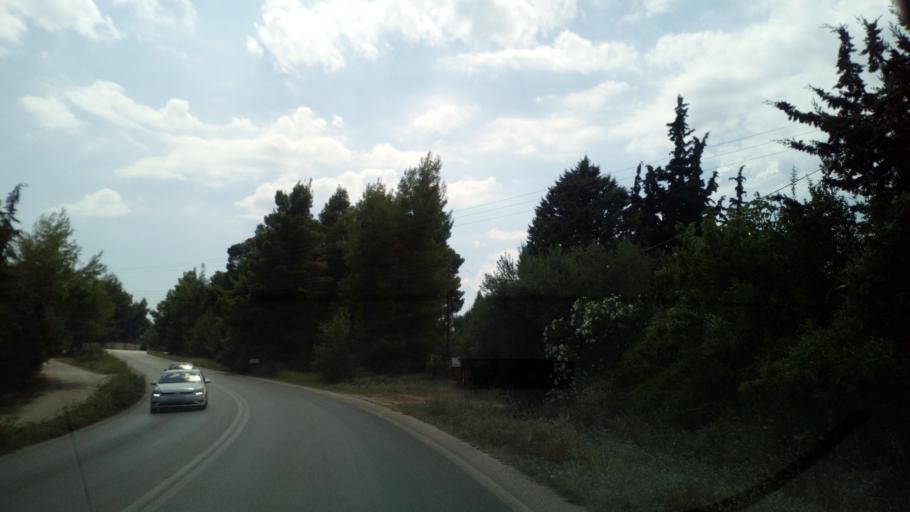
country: GR
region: Central Macedonia
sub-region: Nomos Chalkidikis
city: Nikiti
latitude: 40.2316
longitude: 23.6113
